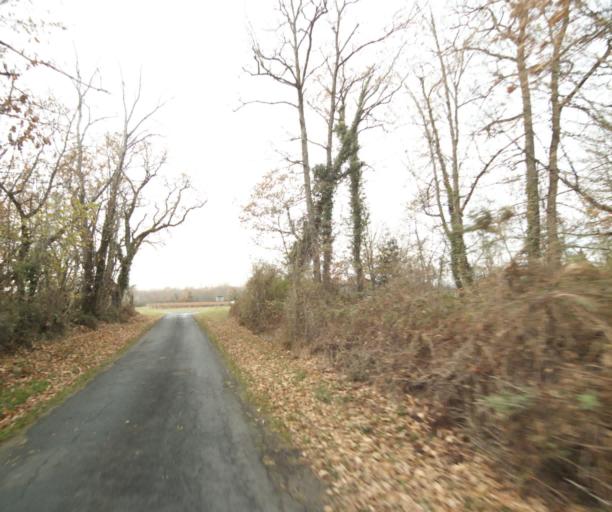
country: FR
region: Poitou-Charentes
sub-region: Departement de la Charente-Maritime
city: Bussac-sur-Charente
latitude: 45.7962
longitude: -0.6051
